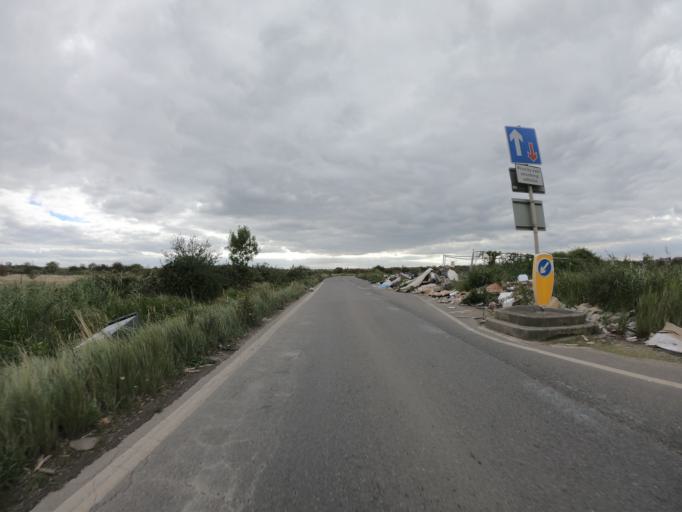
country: GB
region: England
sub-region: Greater London
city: Erith
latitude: 51.4744
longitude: 0.2062
